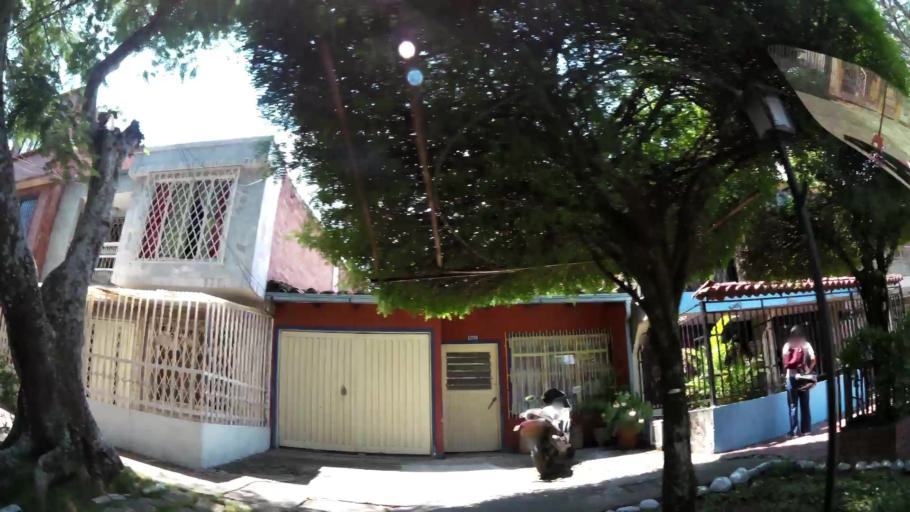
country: CO
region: Valle del Cauca
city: Cali
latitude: 3.4469
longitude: -76.4970
